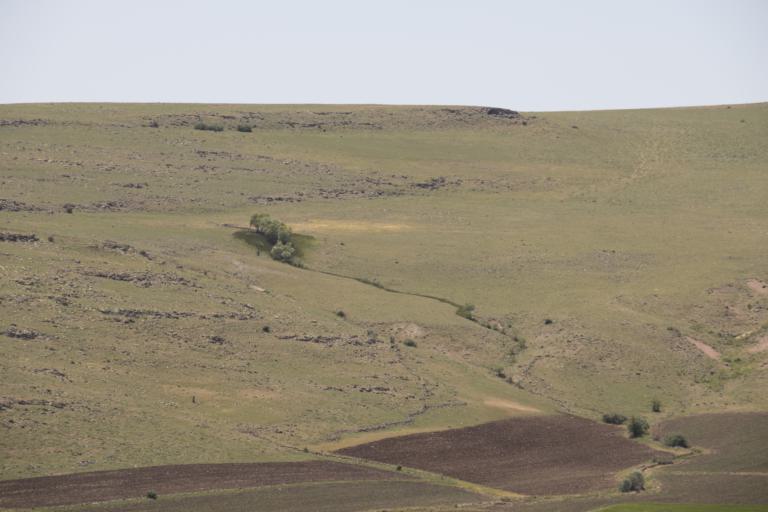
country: TR
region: Kayseri
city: Toklar
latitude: 38.4656
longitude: 36.0780
